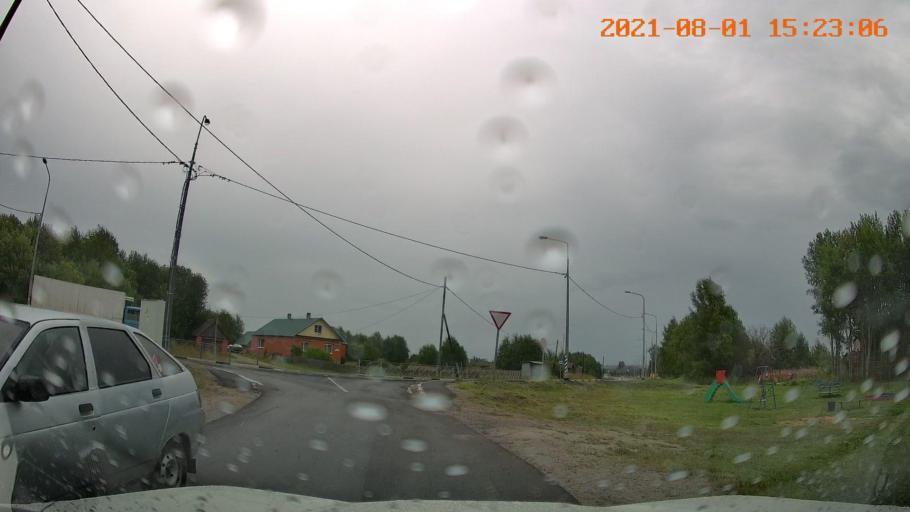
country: RU
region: Republic of Karelia
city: Pudozh
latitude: 61.6689
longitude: 36.3580
